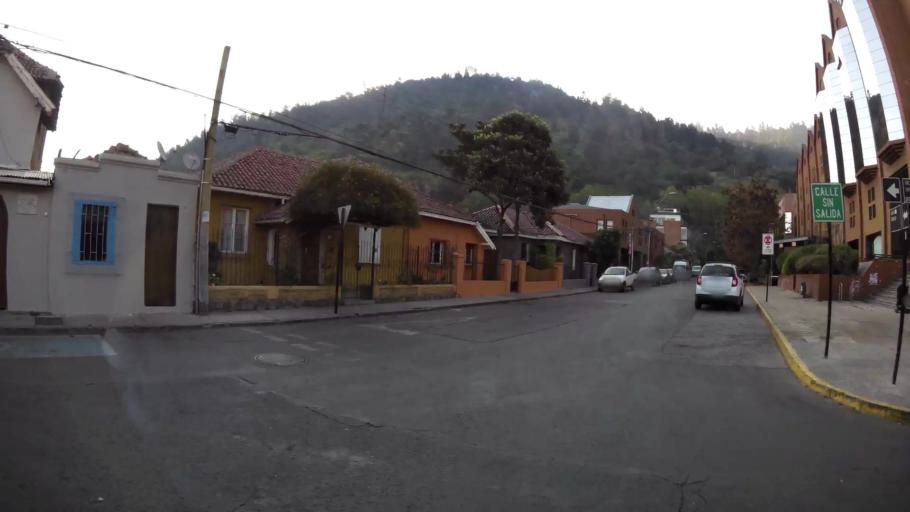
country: CL
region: Santiago Metropolitan
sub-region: Provincia de Santiago
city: Santiago
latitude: -33.4285
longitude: -70.6273
